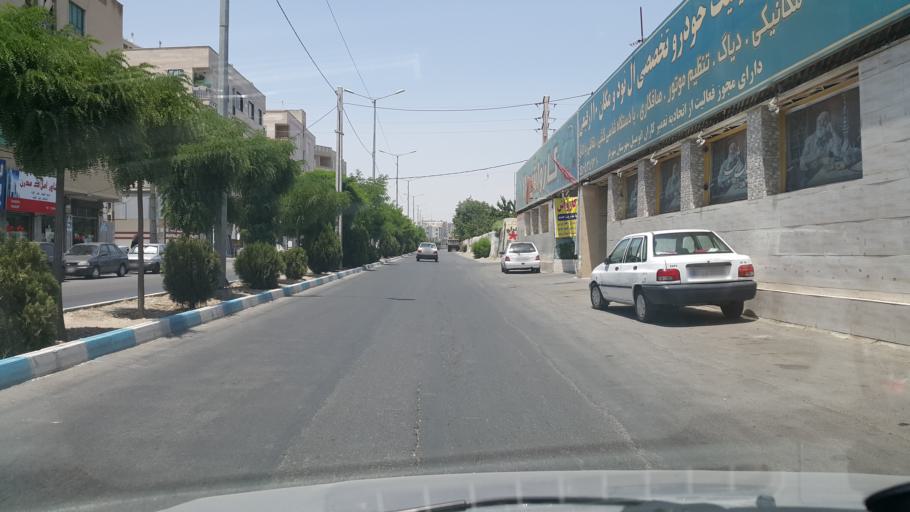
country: IR
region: Tehran
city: Shahre Jadide Andisheh
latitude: 35.6664
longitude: 51.0121
